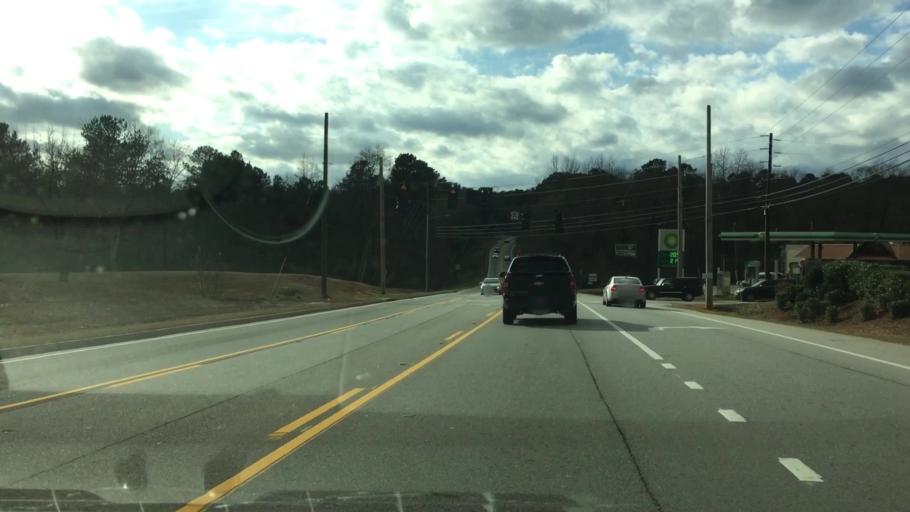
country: US
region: Georgia
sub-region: Henry County
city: McDonough
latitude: 33.4350
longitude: -84.1644
